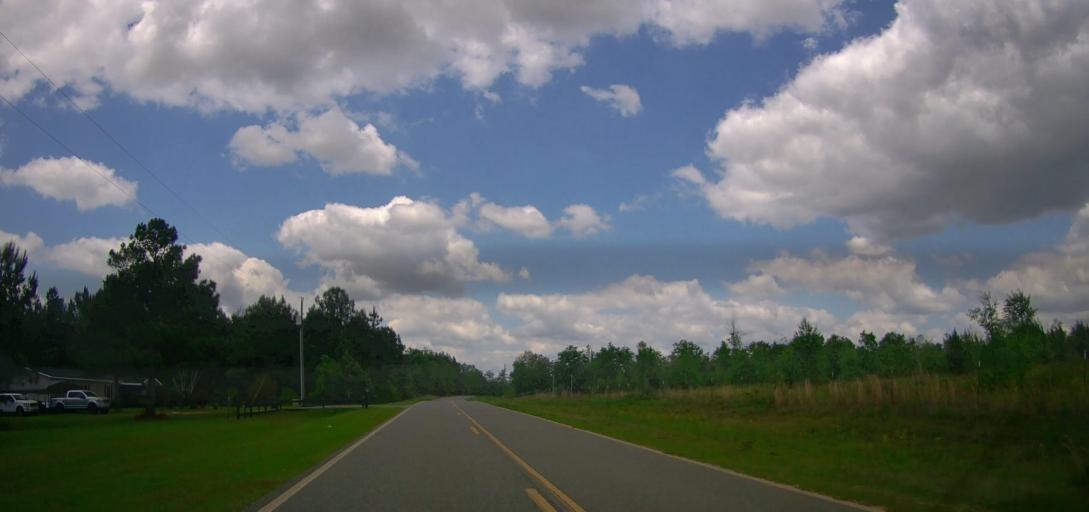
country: US
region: Georgia
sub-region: Laurens County
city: East Dublin
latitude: 32.6092
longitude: -82.8064
